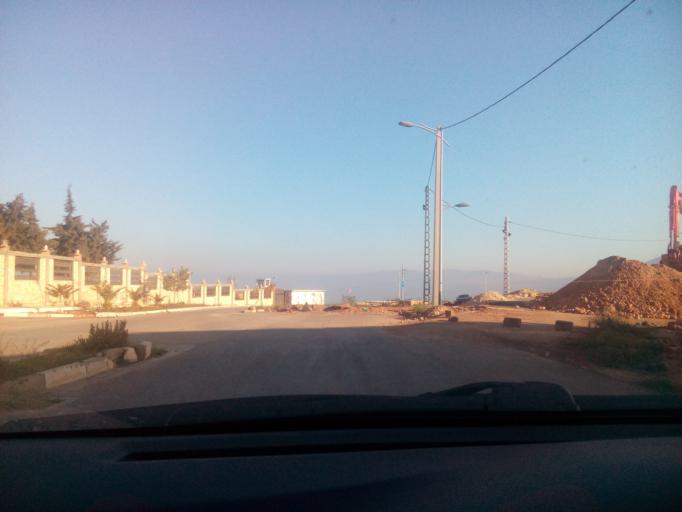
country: DZ
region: Oran
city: Bir el Djir
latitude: 35.7604
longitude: -0.5343
